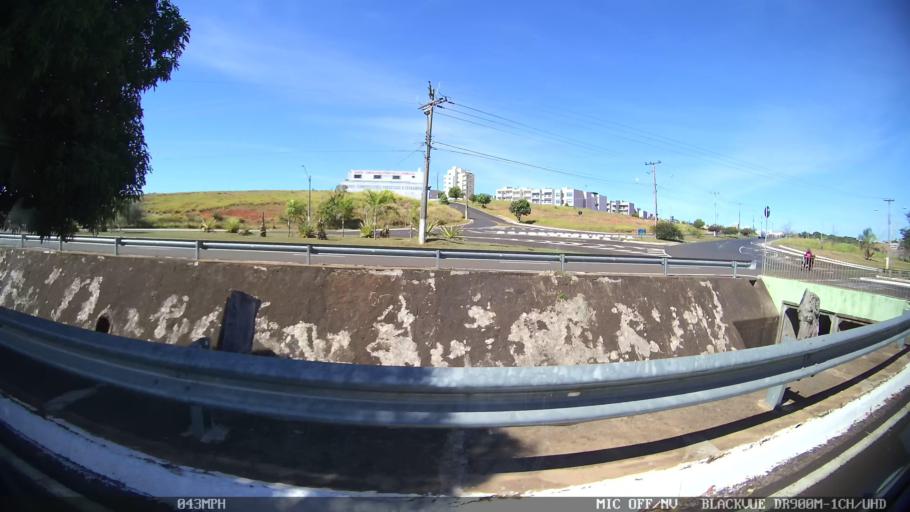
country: BR
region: Sao Paulo
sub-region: Franca
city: Franca
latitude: -20.5334
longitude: -47.3769
